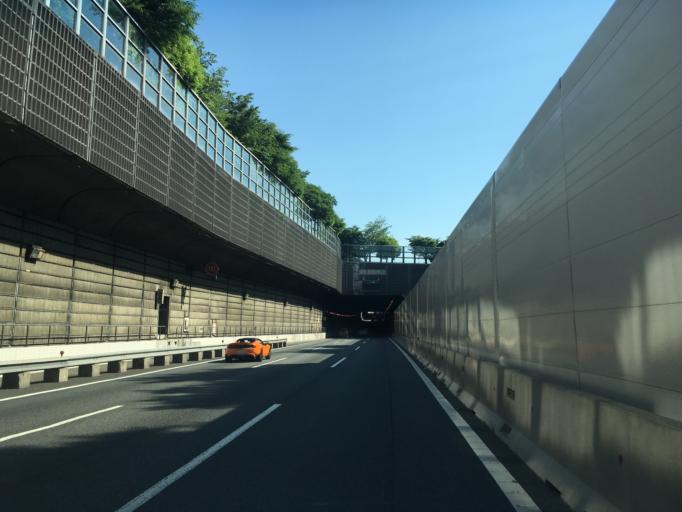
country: JP
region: Saitama
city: Wako
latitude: 35.7639
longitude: 139.5995
